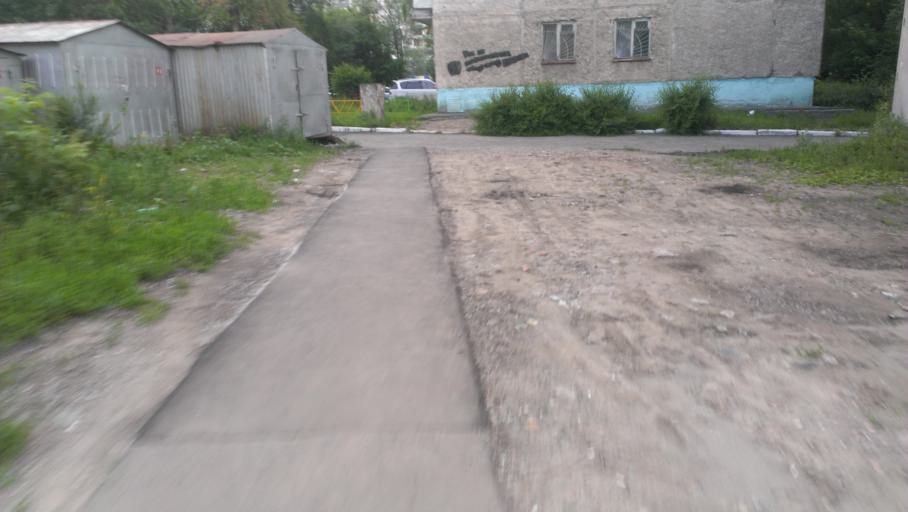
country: RU
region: Altai Krai
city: Novosilikatnyy
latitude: 53.3769
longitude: 83.6779
